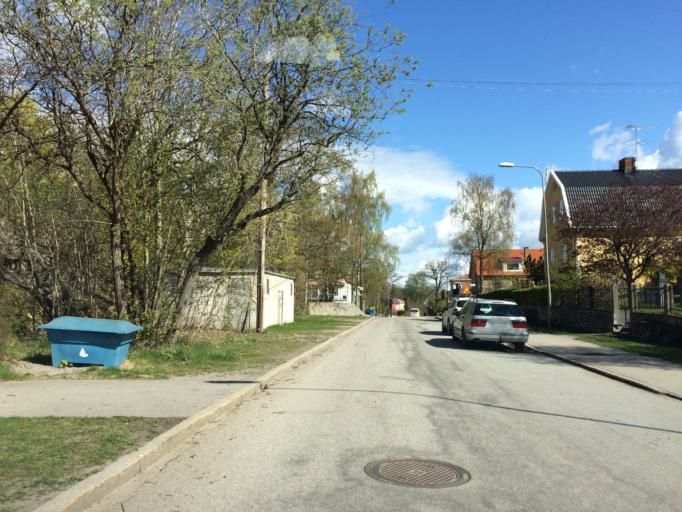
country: SE
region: Stockholm
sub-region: Huddinge Kommun
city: Segeltorp
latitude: 59.2975
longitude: 17.9485
